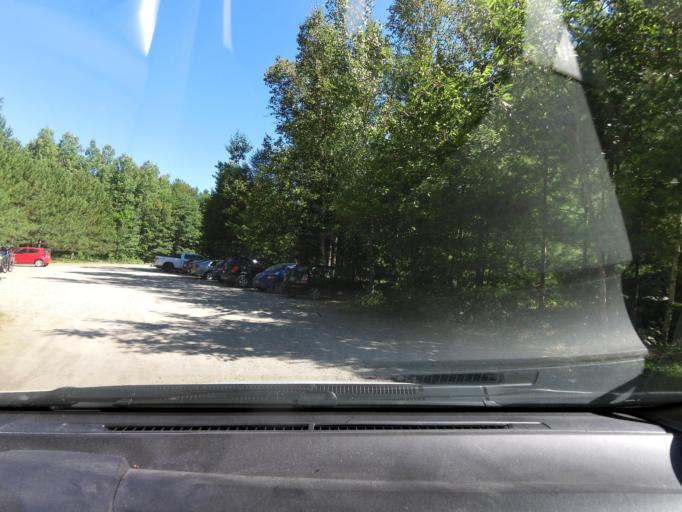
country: CA
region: Quebec
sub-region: Mauricie
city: Becancour
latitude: 46.5542
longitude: -72.4123
